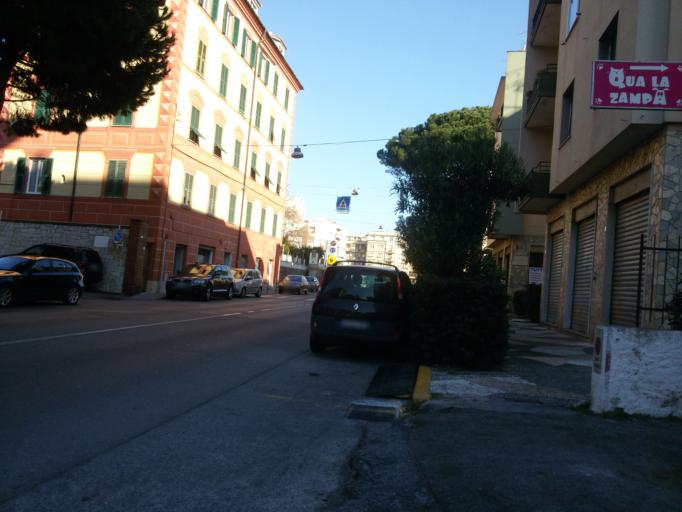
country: IT
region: Liguria
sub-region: Provincia di Savona
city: Savona
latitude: 44.2965
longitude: 8.4626
